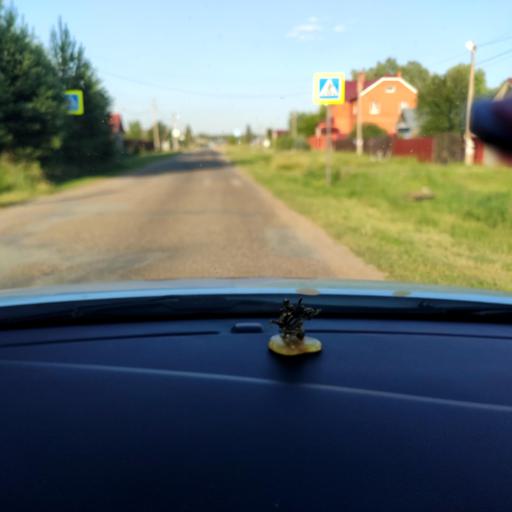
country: RU
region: Tatarstan
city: Pestretsy
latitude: 55.6157
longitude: 49.4926
